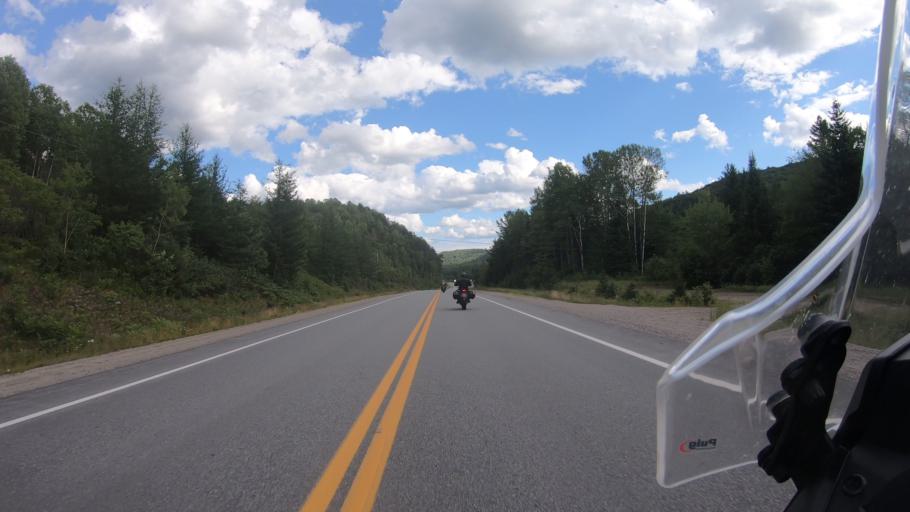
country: CA
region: Quebec
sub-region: Mauricie
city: Saint-Tite
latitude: 47.0030
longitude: -72.9255
